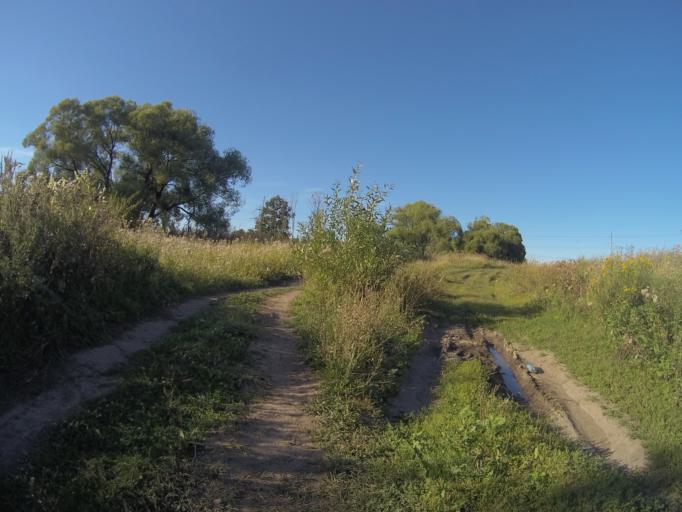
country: RU
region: Vladimir
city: Vladimir
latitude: 56.1860
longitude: 40.3661
